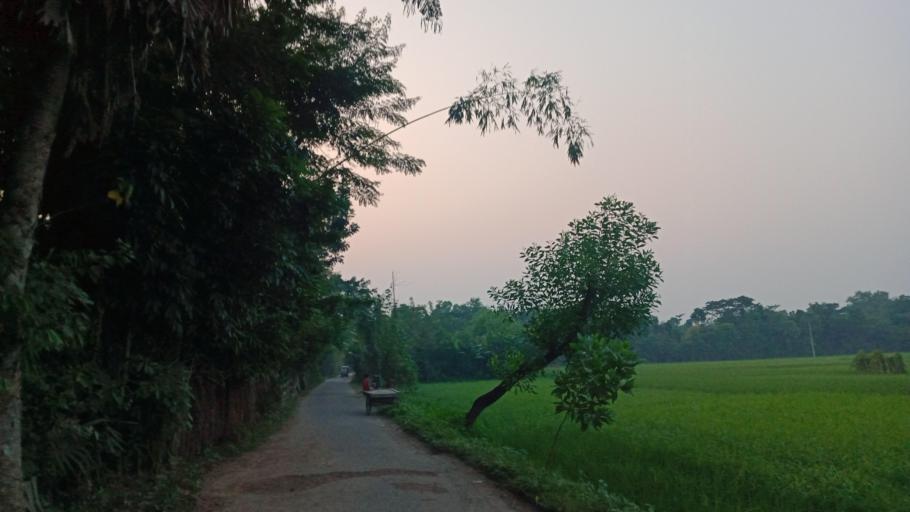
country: BD
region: Chittagong
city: Hajiganj
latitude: 23.3676
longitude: 90.9867
